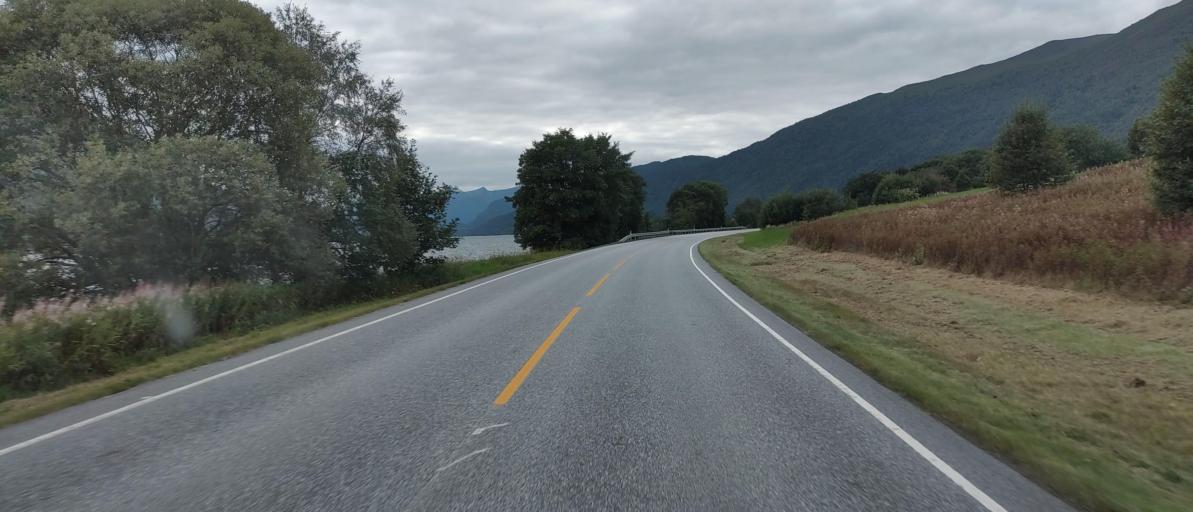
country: NO
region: More og Romsdal
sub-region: Rauma
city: Andalsnes
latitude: 62.5764
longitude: 7.7604
